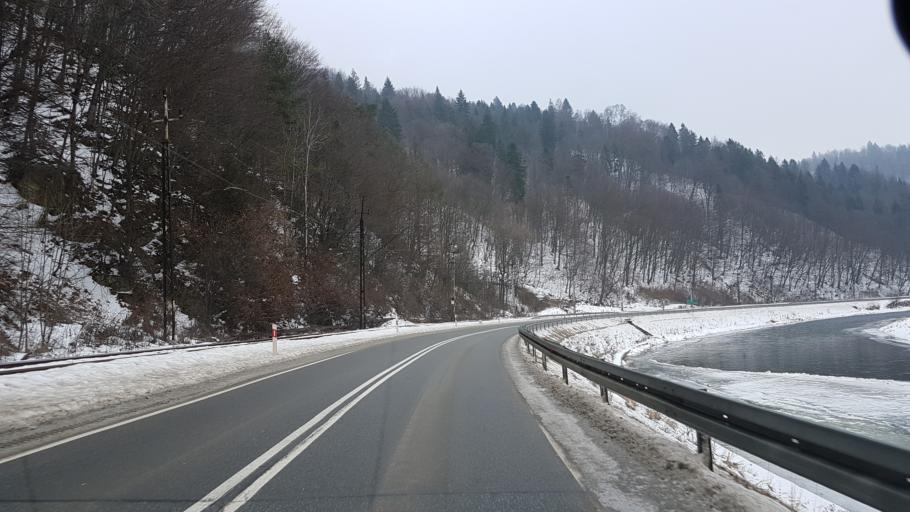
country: PL
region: Lesser Poland Voivodeship
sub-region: Powiat nowosadecki
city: Piwniczna-Zdroj
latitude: 49.4011
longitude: 20.7579
